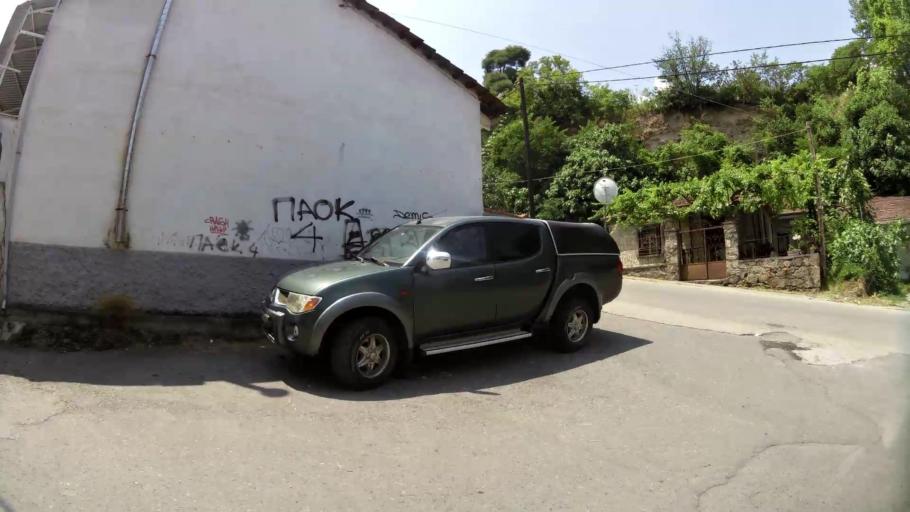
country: GR
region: Central Macedonia
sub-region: Nomos Imathias
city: Veroia
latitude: 40.5166
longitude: 22.1997
